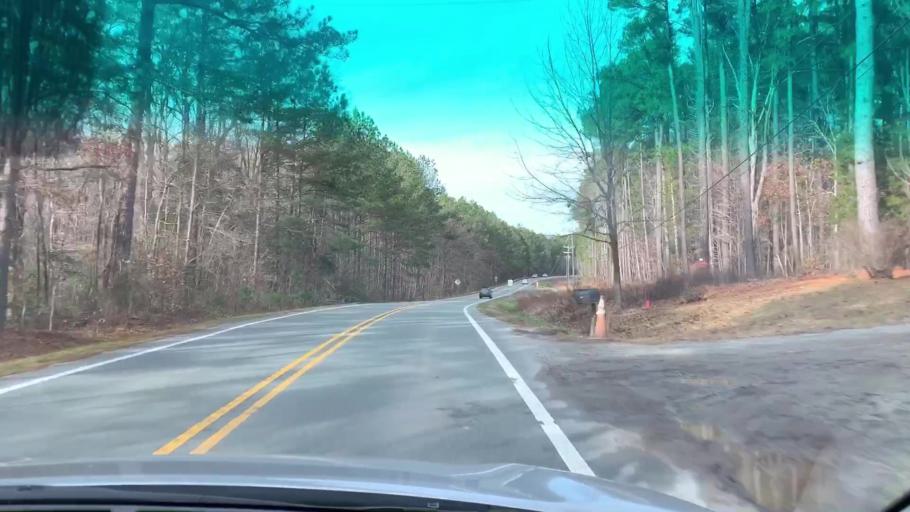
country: US
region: North Carolina
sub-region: Wake County
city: Green Level
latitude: 35.8497
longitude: -78.9336
